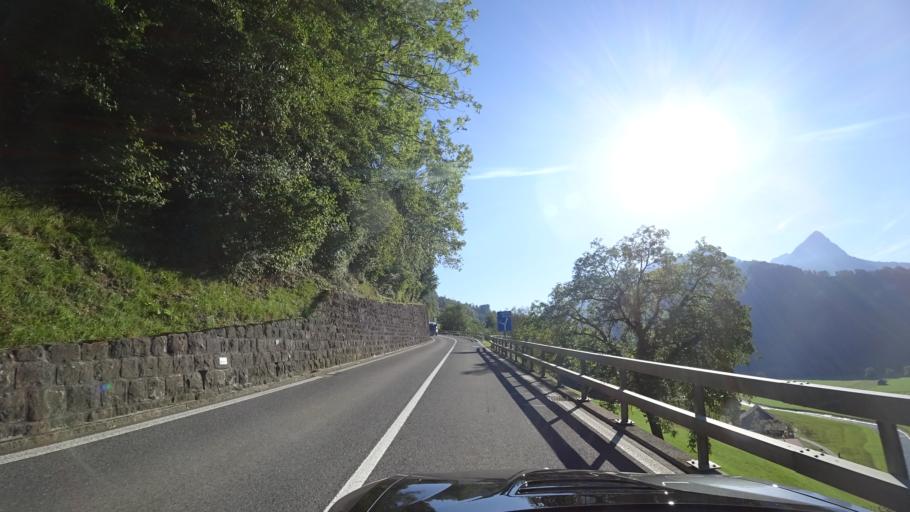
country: CH
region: Obwalden
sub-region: Obwalden
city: Giswil
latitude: 46.8274
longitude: 8.1847
